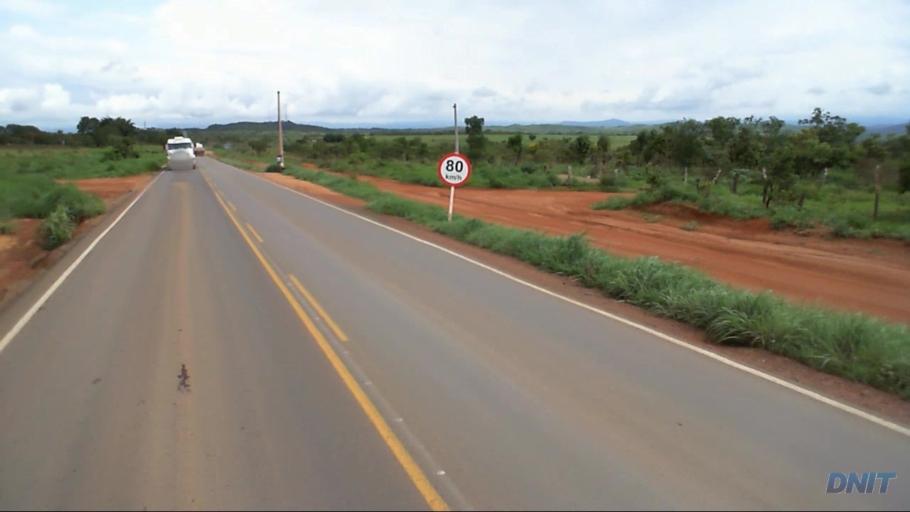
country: BR
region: Goias
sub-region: Padre Bernardo
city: Padre Bernardo
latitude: -15.2478
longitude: -48.2694
